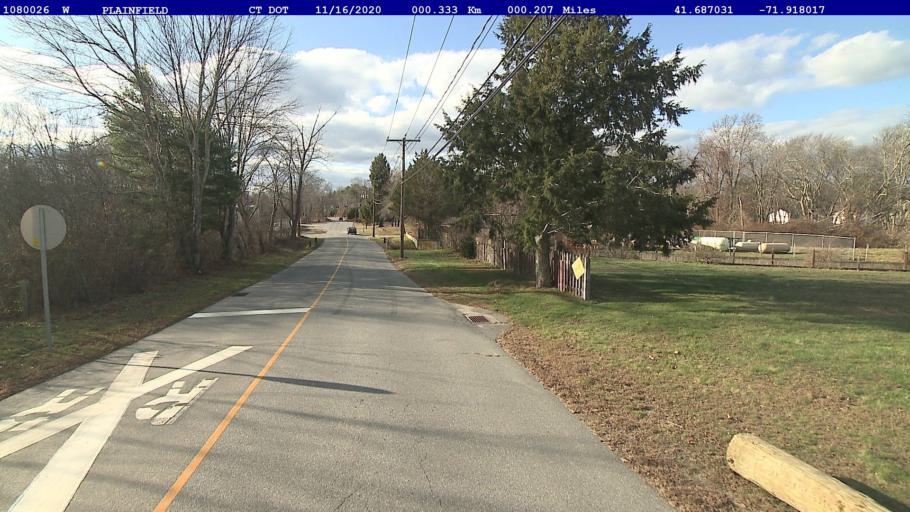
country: US
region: Connecticut
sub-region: Windham County
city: Plainfield
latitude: 41.6870
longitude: -71.9180
